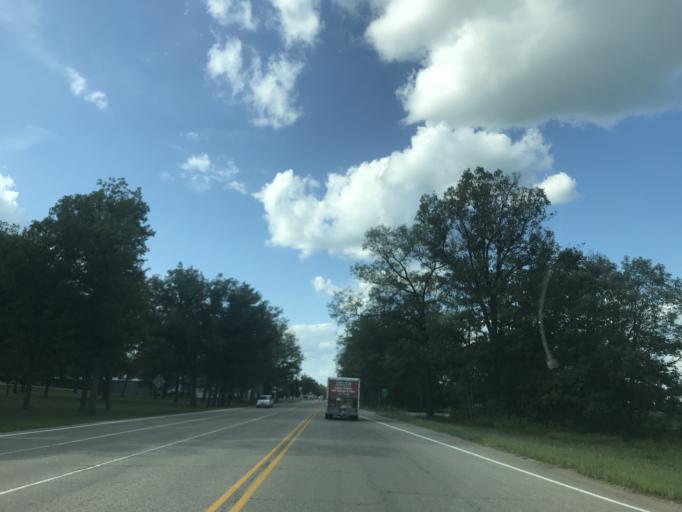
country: US
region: Michigan
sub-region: Newaygo County
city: Newaygo
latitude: 43.4820
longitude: -85.7734
